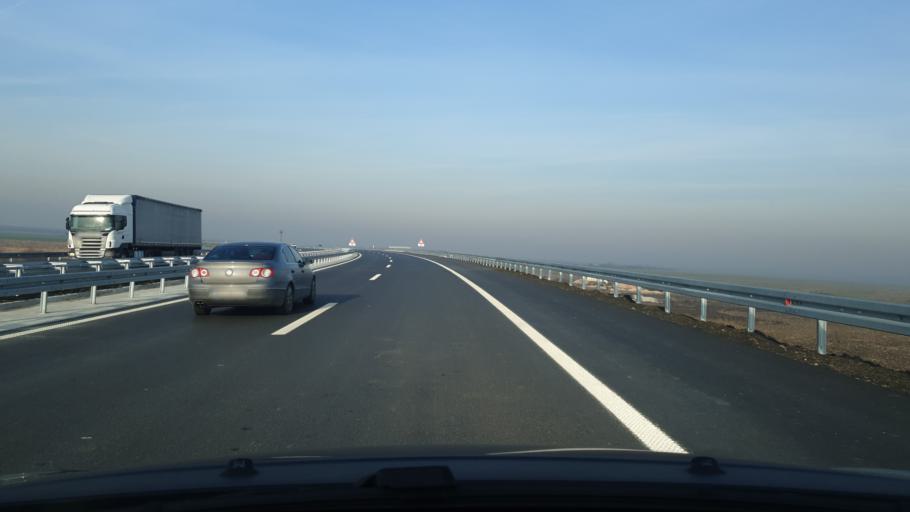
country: RS
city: Baric
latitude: 44.6878
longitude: 20.2673
